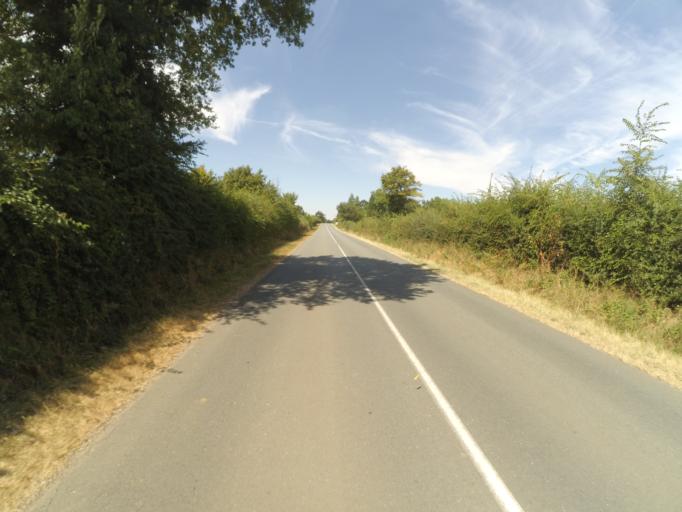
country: FR
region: Poitou-Charentes
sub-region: Departement de la Vienne
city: Usson-du-Poitou
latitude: 46.3065
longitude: 0.4982
